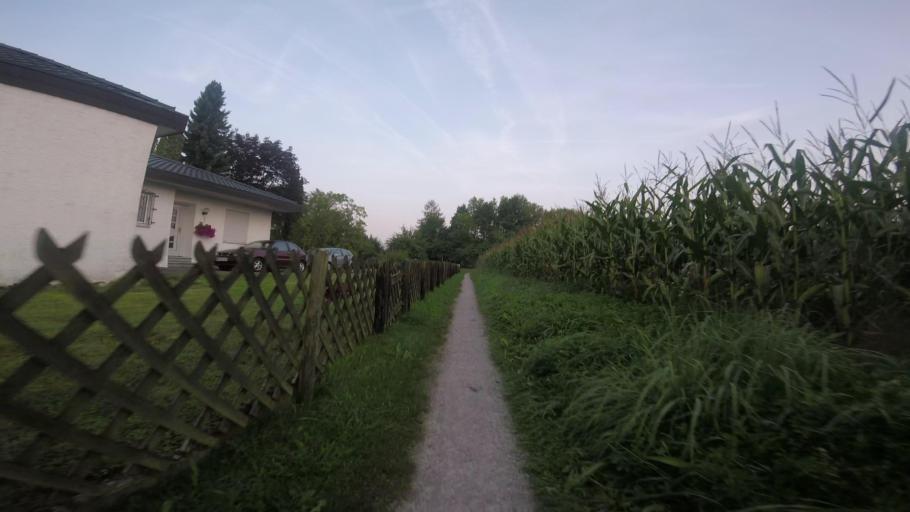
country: DE
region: Baden-Wuerttemberg
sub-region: Regierungsbezirk Stuttgart
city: Aspach
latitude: 48.9701
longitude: 9.3917
